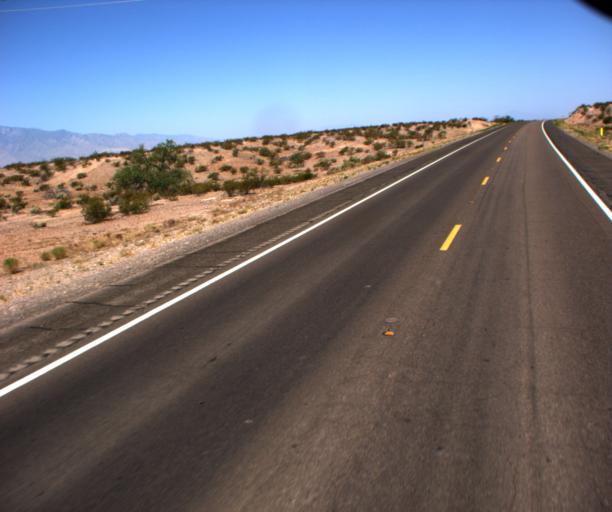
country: US
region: Arizona
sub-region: Graham County
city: Safford
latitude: 32.8027
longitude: -109.5751
